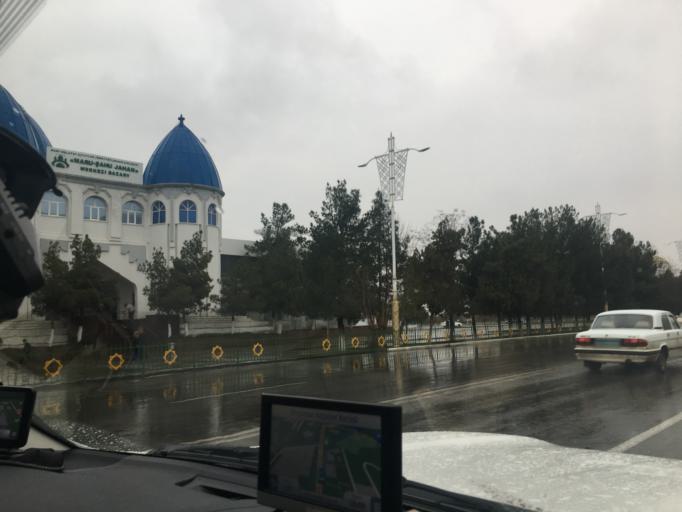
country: TM
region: Mary
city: Mary
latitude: 37.5920
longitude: 61.8449
